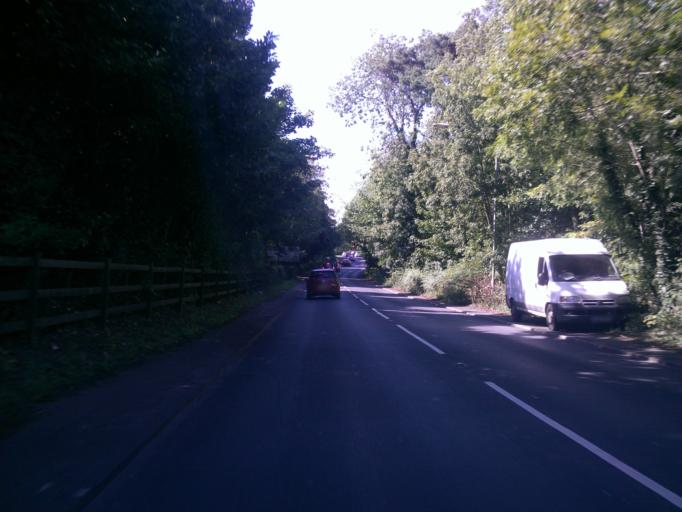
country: GB
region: England
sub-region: Essex
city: Rowhedge
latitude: 51.8796
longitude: 0.9541
